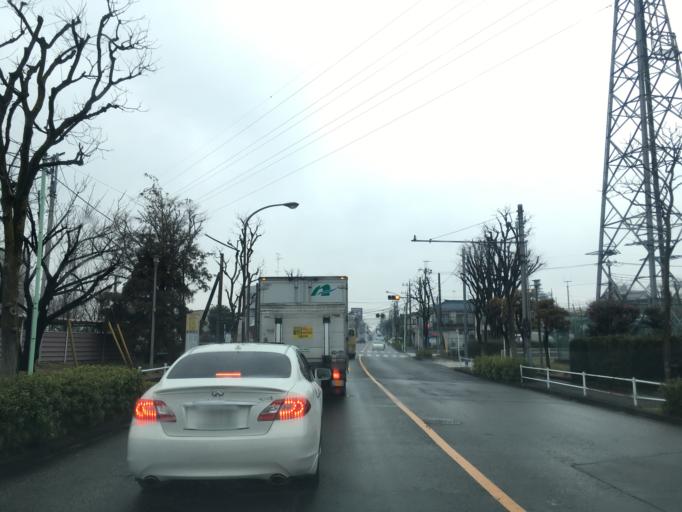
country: JP
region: Tokyo
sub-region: Machida-shi
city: Machida
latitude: 35.5615
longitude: 139.4222
